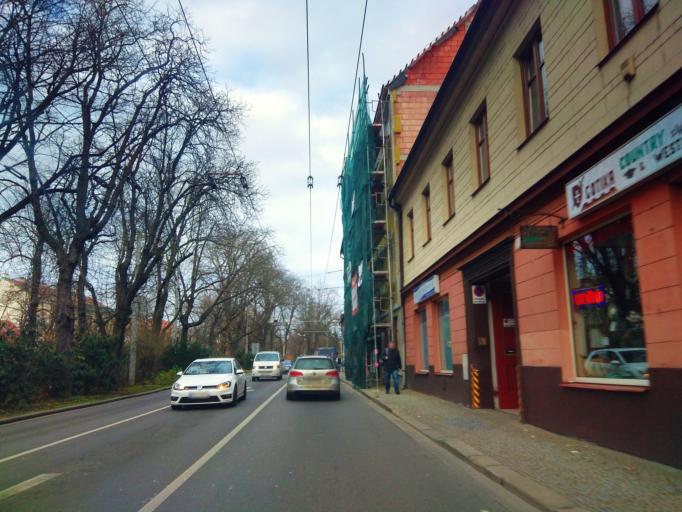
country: CZ
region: Jihocesky
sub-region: Okres Ceske Budejovice
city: Ceske Budejovice
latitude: 48.9757
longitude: 14.4792
